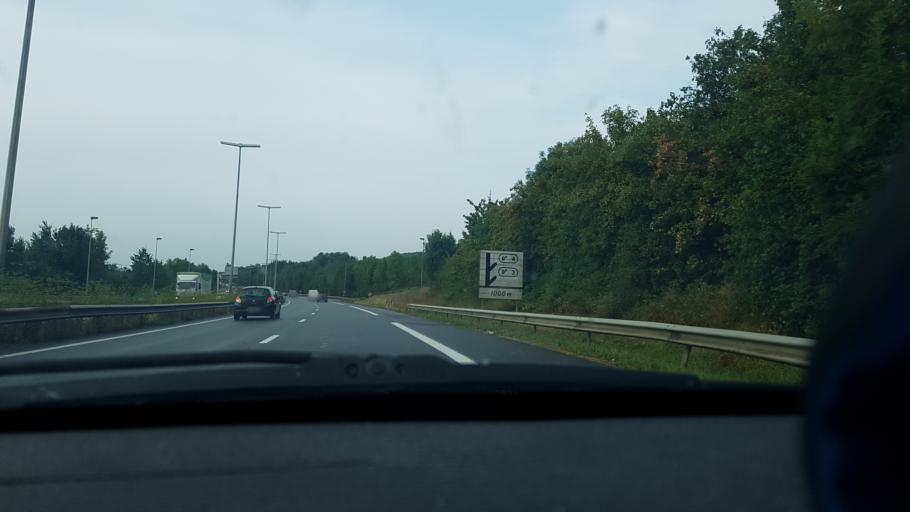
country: FR
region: Lorraine
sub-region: Departement de Meurthe-et-Moselle
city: Vandoeuvre-les-Nancy
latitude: 48.6517
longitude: 6.1818
